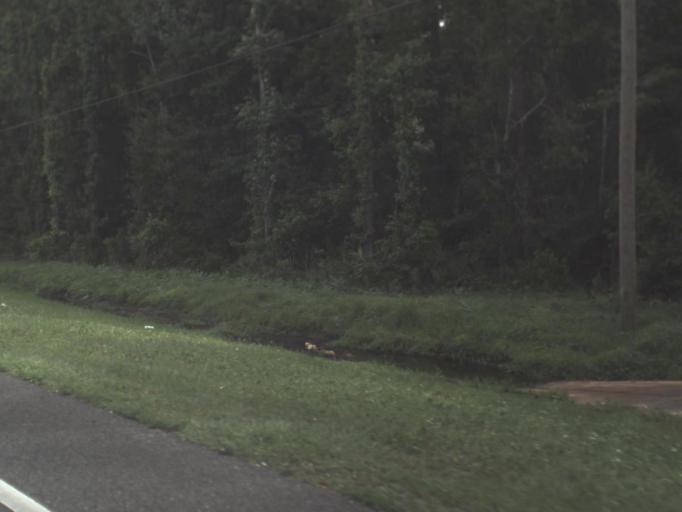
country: US
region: Florida
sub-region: Clay County
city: Orange Park
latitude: 30.1222
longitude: -81.7043
